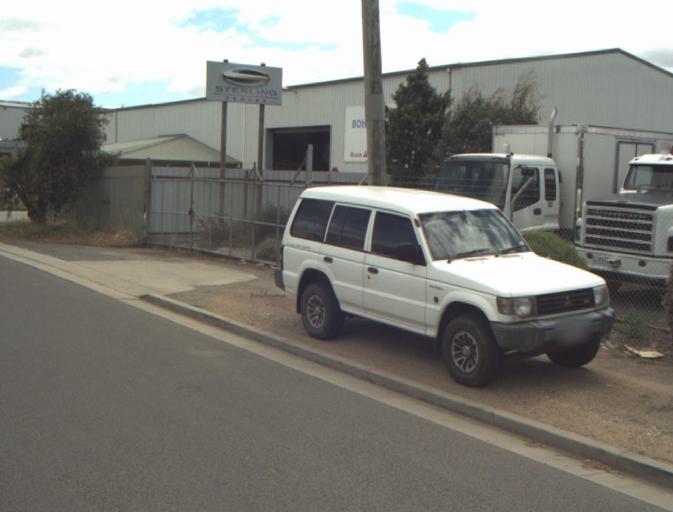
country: AU
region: Tasmania
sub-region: Launceston
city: Launceston
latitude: -41.4250
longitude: 147.1253
